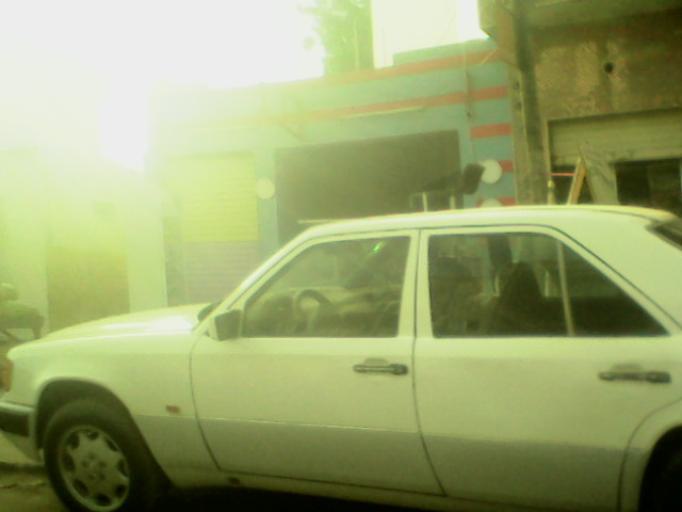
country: SN
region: Diourbel
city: Touba
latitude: 14.8563
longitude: -15.8793
